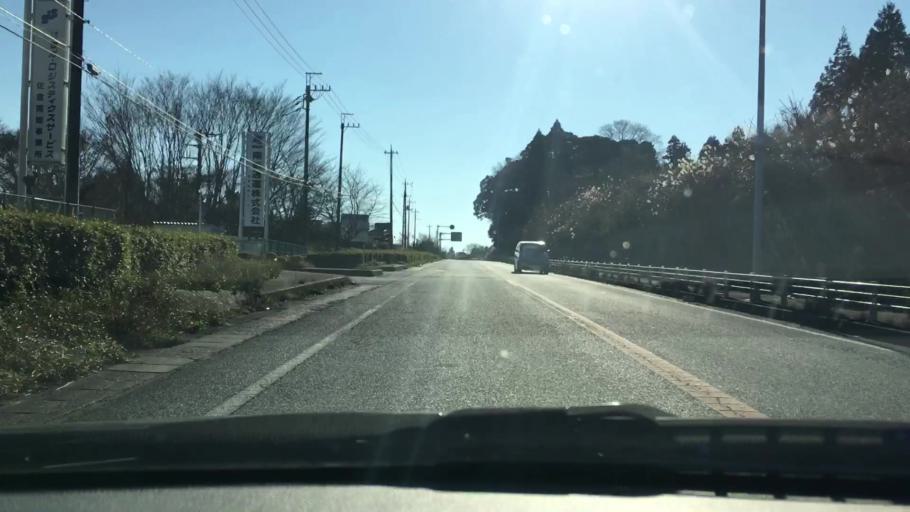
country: JP
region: Chiba
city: Sakura
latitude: 35.6924
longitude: 140.2450
